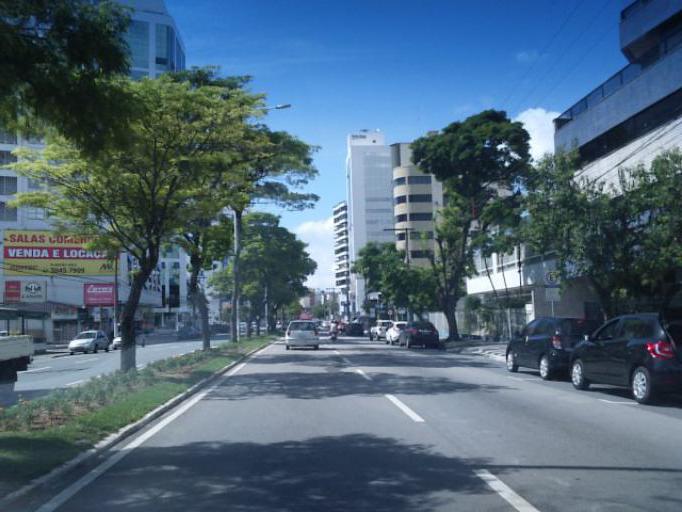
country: BR
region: Santa Catarina
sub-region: Itajai
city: Itajai
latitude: -26.9090
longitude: -48.6608
